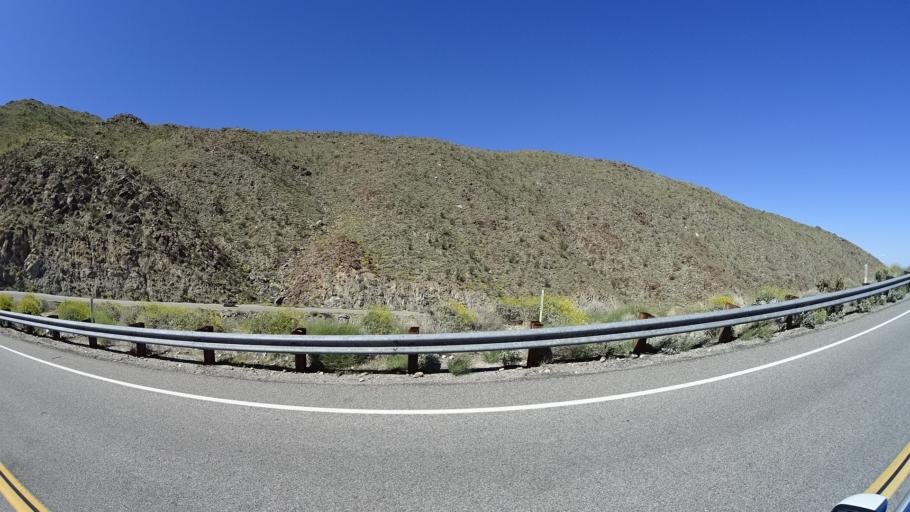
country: US
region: California
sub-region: San Diego County
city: Borrego Springs
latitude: 33.2234
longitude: -116.4233
